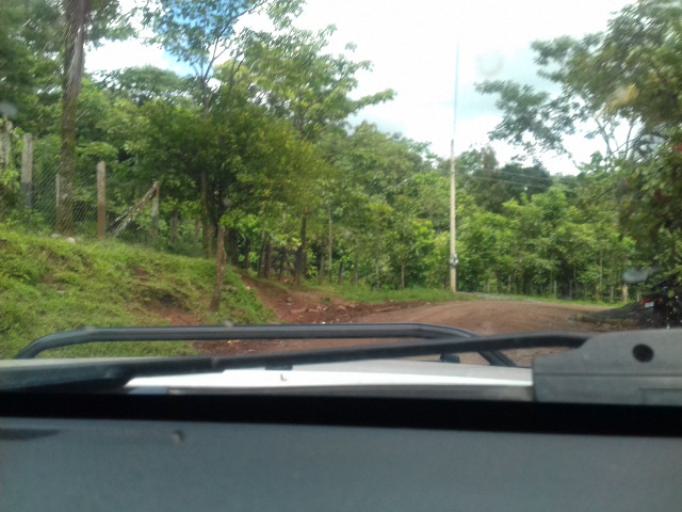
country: NI
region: Matagalpa
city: Rio Blanco
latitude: 12.9993
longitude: -85.1993
